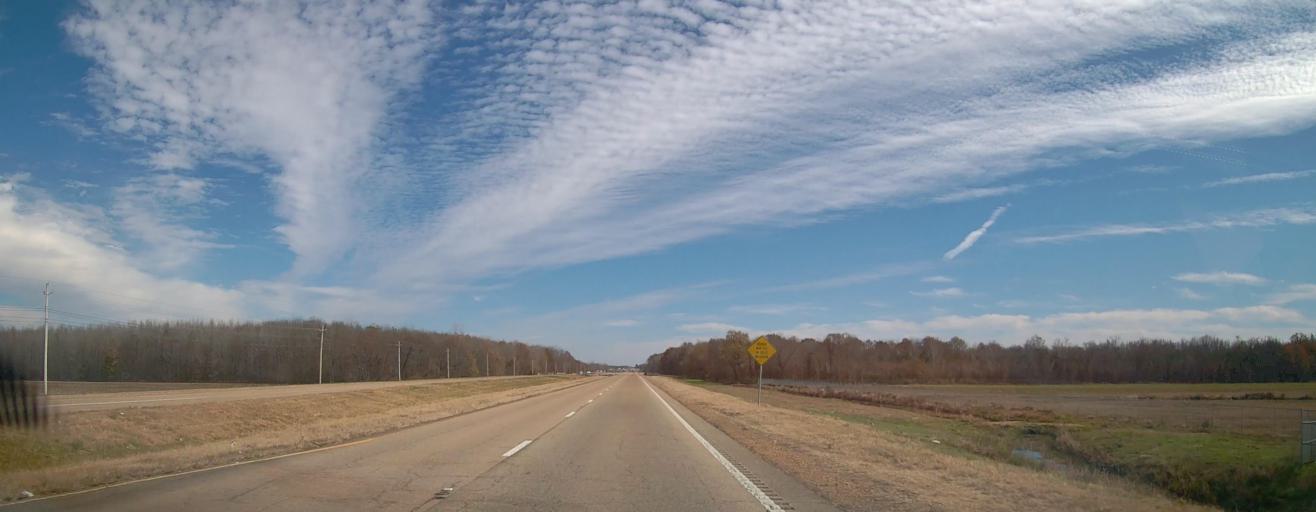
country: US
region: Mississippi
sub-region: Alcorn County
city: Corinth
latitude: 34.9311
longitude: -88.6054
